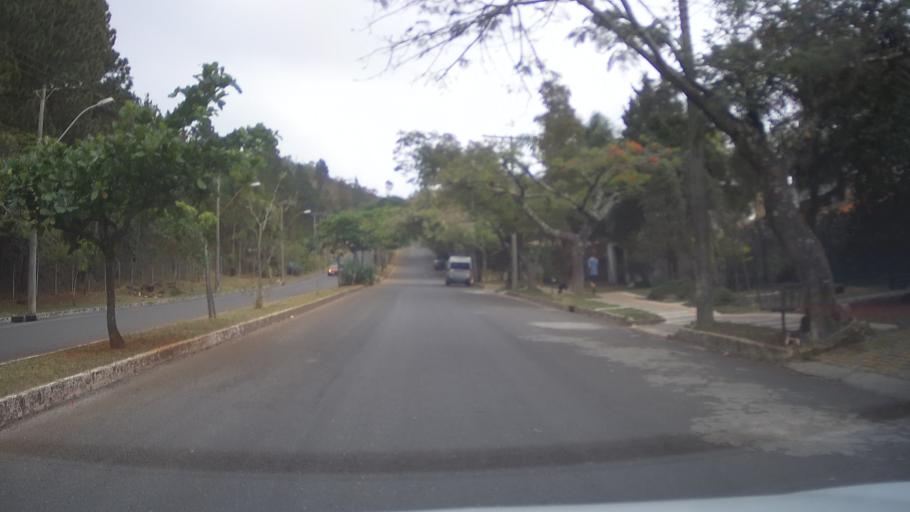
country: BR
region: Minas Gerais
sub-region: Belo Horizonte
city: Belo Horizonte
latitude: -19.9604
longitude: -43.9164
